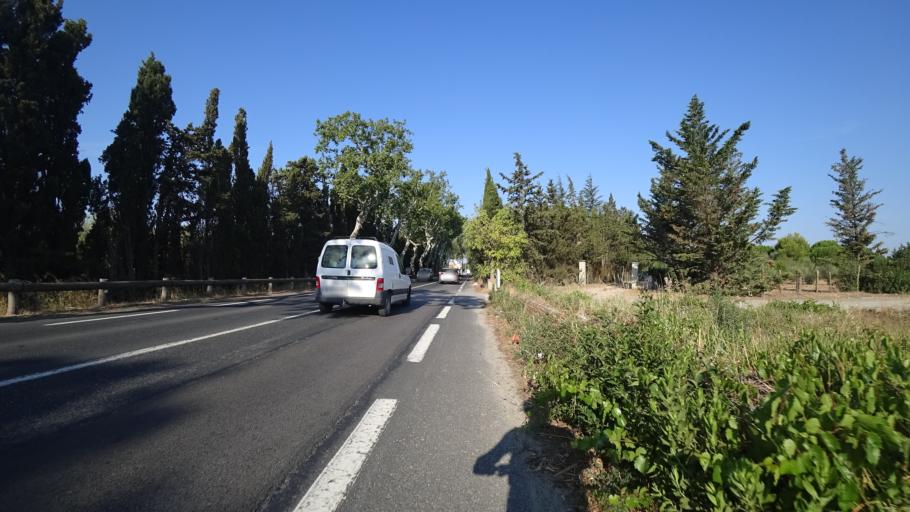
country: FR
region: Languedoc-Roussillon
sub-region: Departement des Pyrenees-Orientales
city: Bompas
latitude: 42.7300
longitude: 2.9199
